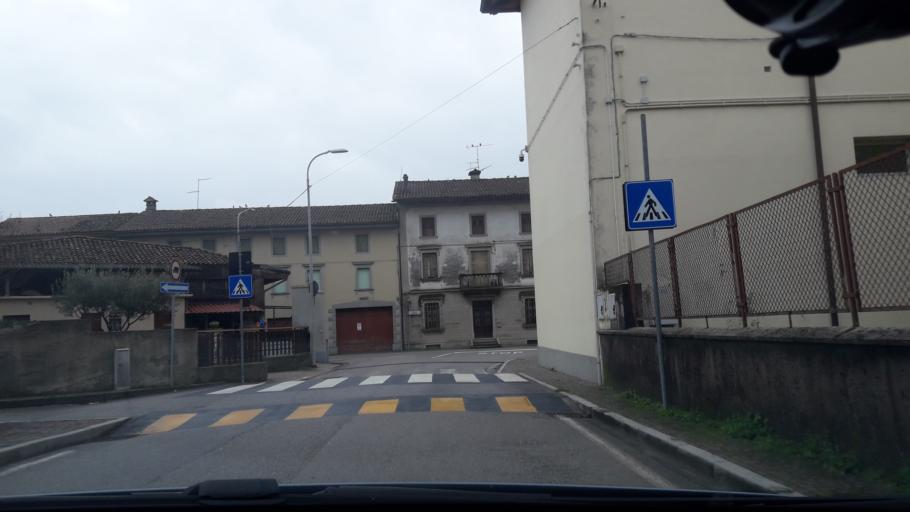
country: IT
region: Friuli Venezia Giulia
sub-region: Provincia di Udine
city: Colloredo di Prato
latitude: 46.0514
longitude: 13.1421
